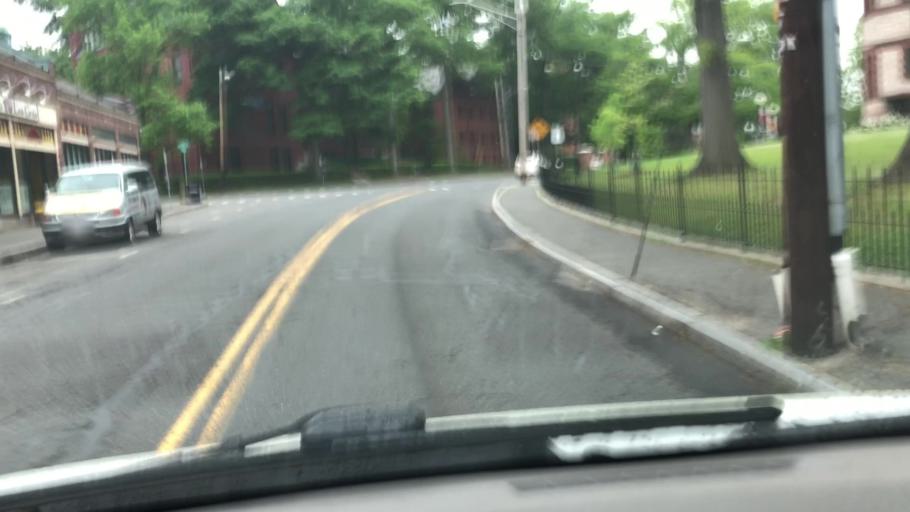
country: US
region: Massachusetts
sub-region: Hampshire County
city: Northampton
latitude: 42.3164
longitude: -72.6365
